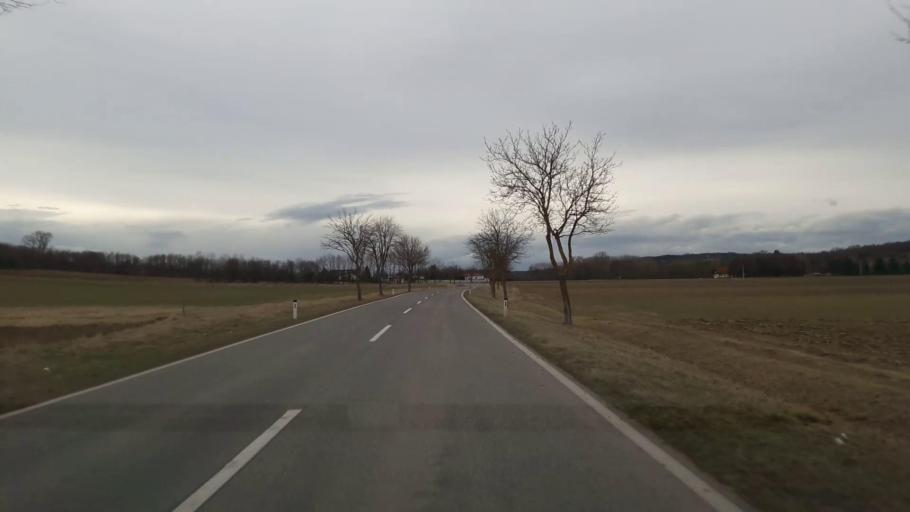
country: AT
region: Burgenland
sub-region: Politischer Bezirk Oberpullendorf
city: Lutzmannsburg
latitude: 47.4577
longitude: 16.5845
